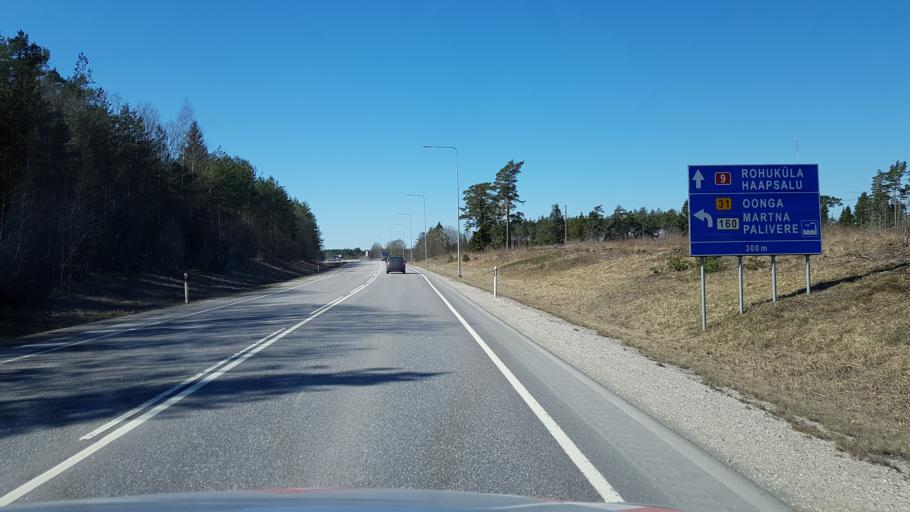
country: EE
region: Laeaene
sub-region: Lihula vald
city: Lihula
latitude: 58.9734
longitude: 23.9071
